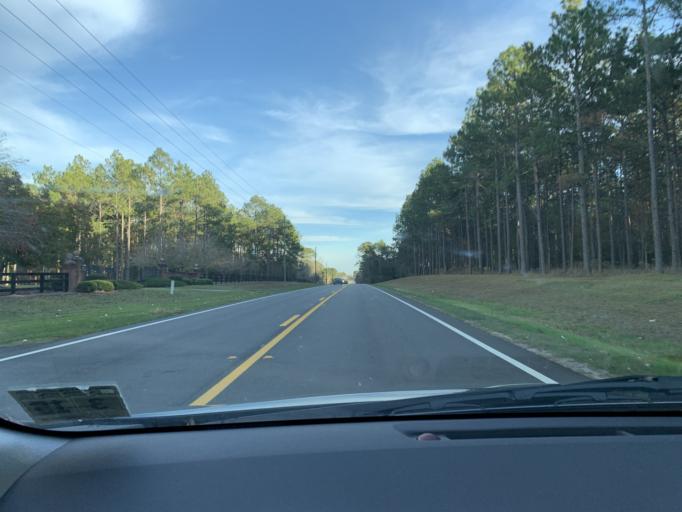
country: US
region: Georgia
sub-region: Irwin County
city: Ocilla
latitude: 31.5827
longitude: -83.0687
